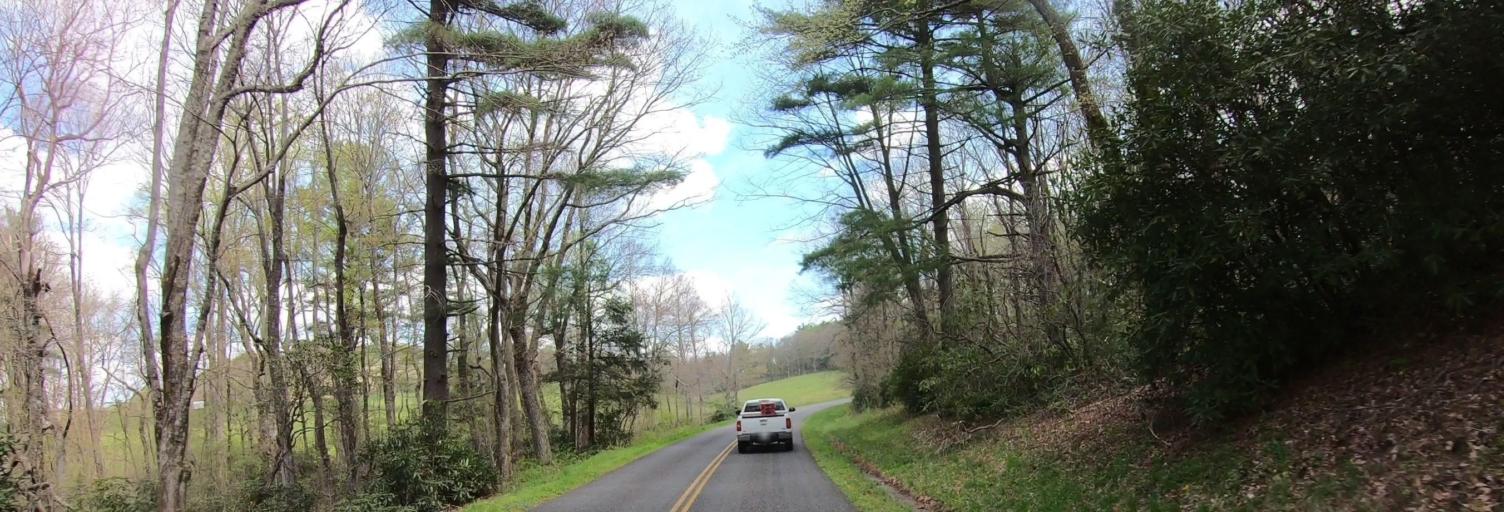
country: US
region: Virginia
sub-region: Carroll County
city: Cana
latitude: 36.6562
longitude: -80.7021
